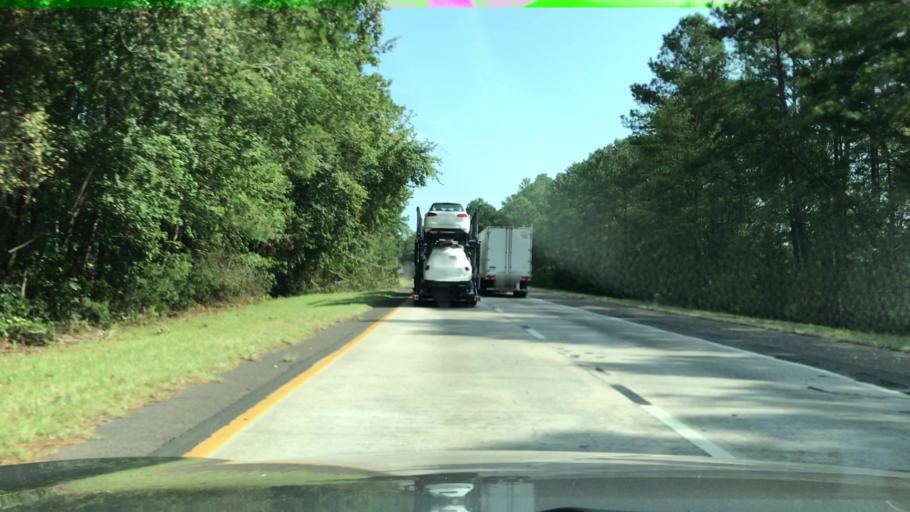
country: US
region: South Carolina
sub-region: Colleton County
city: Walterboro
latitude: 32.8247
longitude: -80.7501
